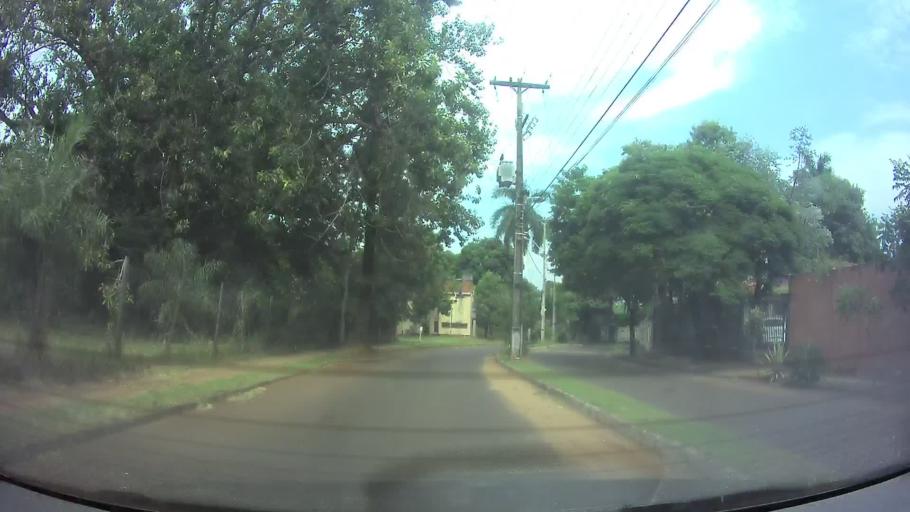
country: PY
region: Central
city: San Lorenzo
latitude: -25.2910
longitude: -57.5107
